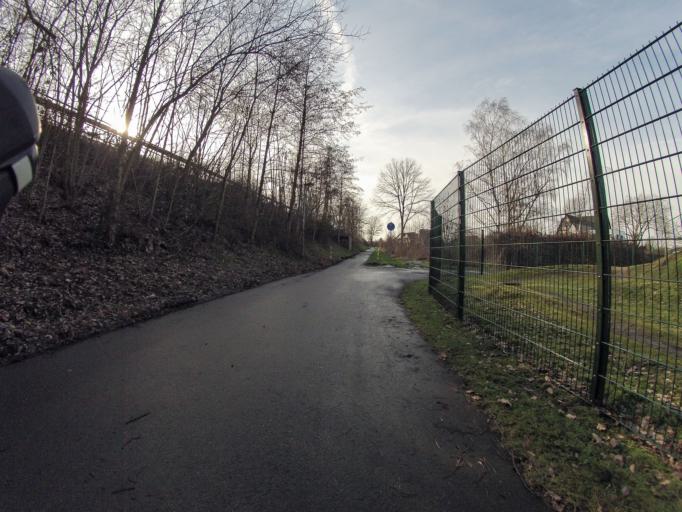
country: DE
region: North Rhine-Westphalia
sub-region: Regierungsbezirk Munster
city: Rheine
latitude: 52.2688
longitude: 7.4537
